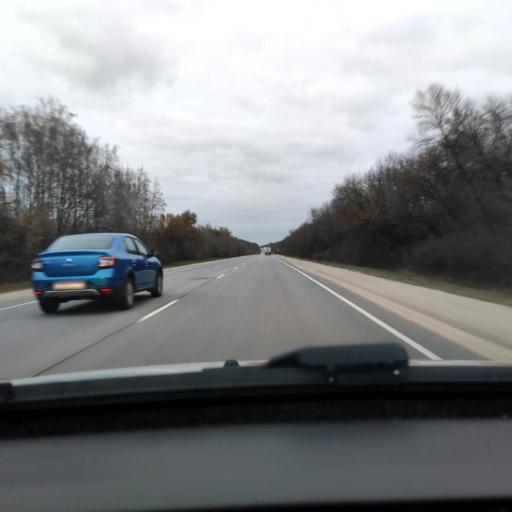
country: RU
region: Lipetsk
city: Borinskoye
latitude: 52.3795
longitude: 39.2177
